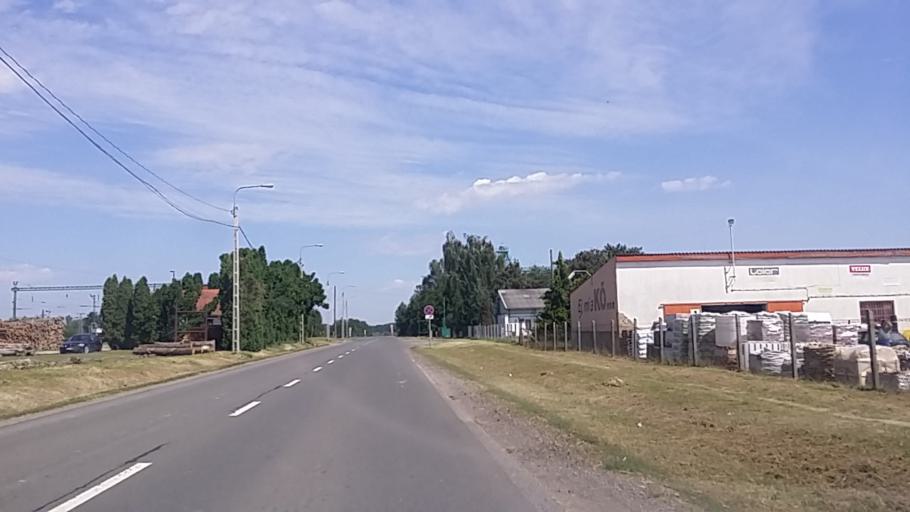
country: HU
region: Baranya
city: Sasd
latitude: 46.2609
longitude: 18.1057
